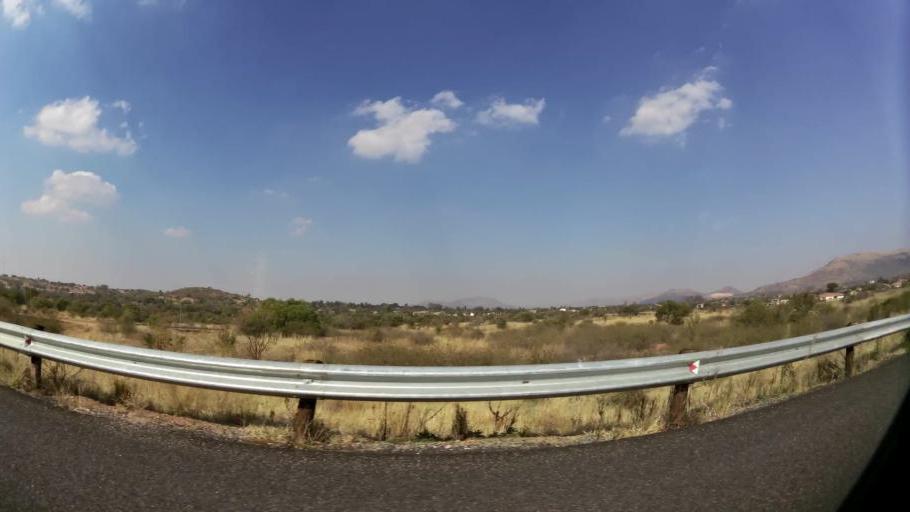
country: ZA
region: North-West
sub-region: Bojanala Platinum District Municipality
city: Rustenburg
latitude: -25.5815
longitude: 27.1350
